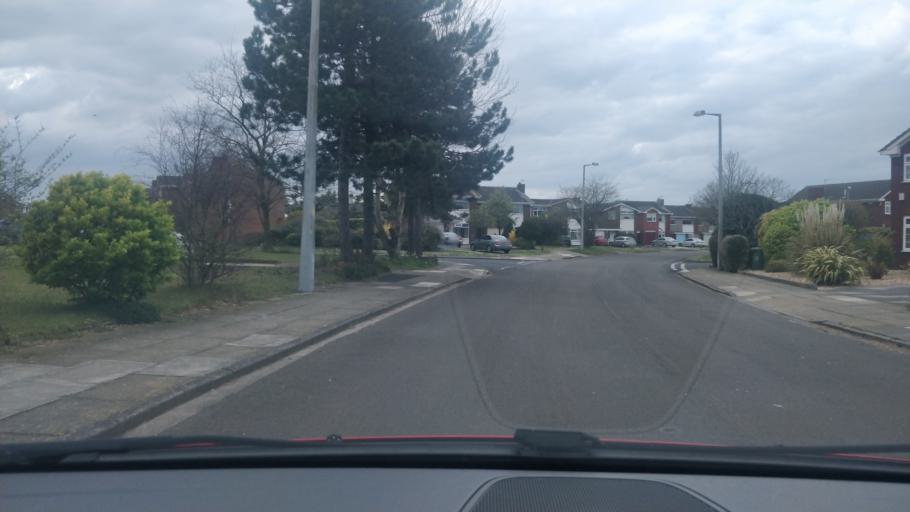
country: GB
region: England
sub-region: Sefton
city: Formby
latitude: 53.5979
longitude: -3.0512
